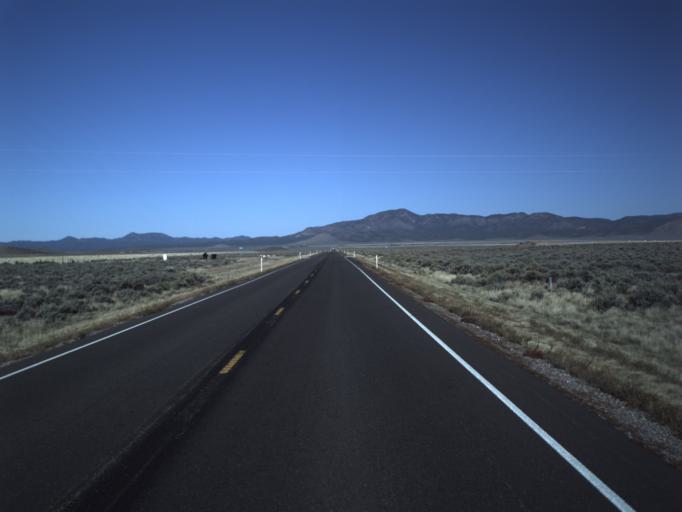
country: US
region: Utah
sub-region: Washington County
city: Enterprise
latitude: 37.7669
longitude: -113.8187
